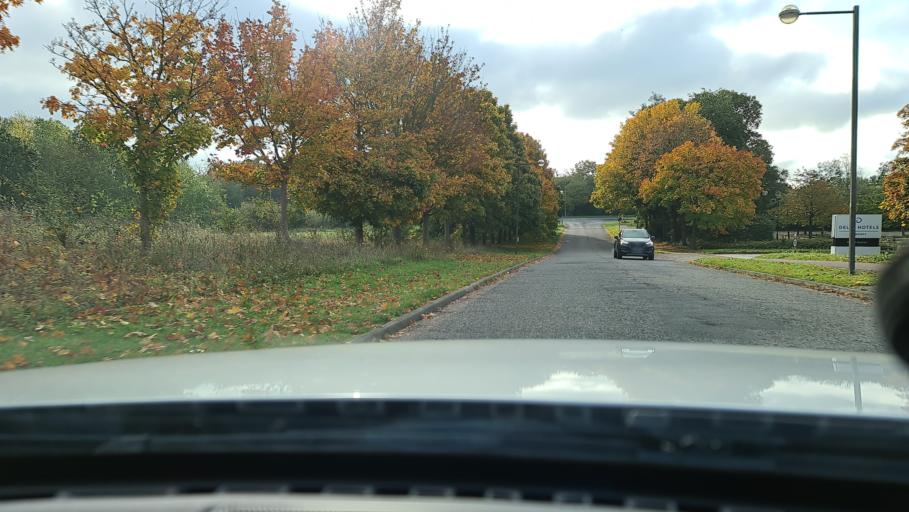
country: GB
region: England
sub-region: Milton Keynes
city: Simpson
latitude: 52.0247
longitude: -0.7000
